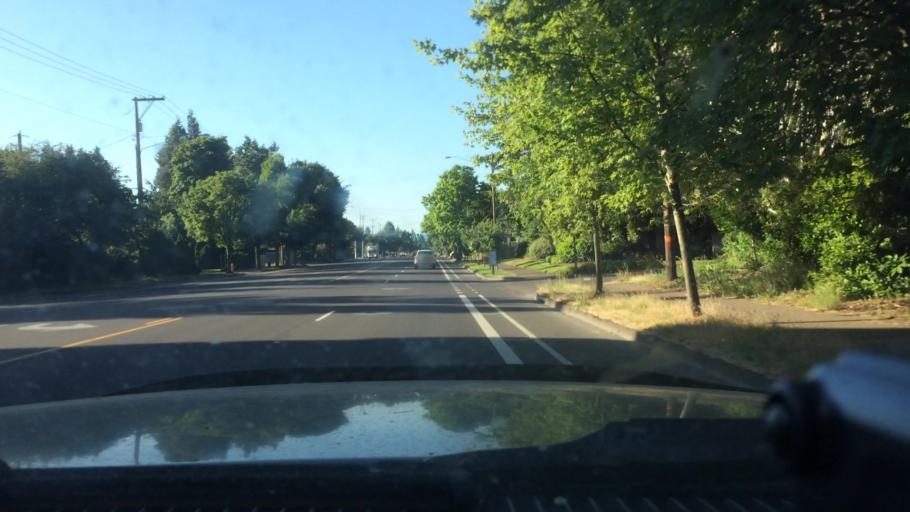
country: US
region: Oregon
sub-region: Lane County
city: Eugene
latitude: 44.0838
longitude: -123.1232
